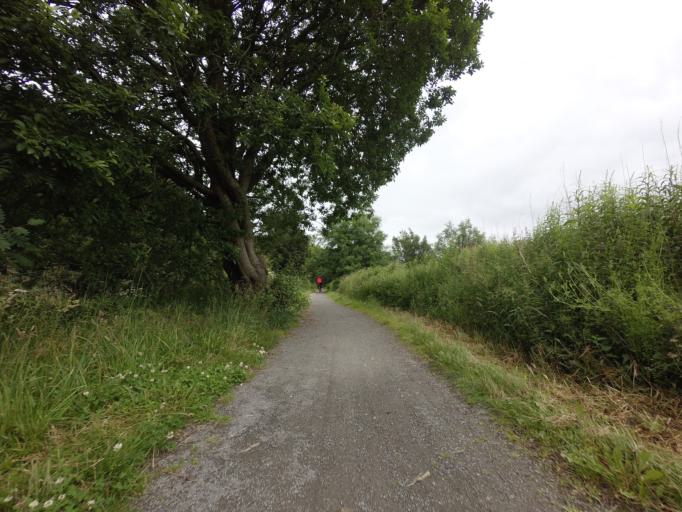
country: GB
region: Scotland
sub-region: Aberdeenshire
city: Mintlaw
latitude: 57.5182
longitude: -2.1304
